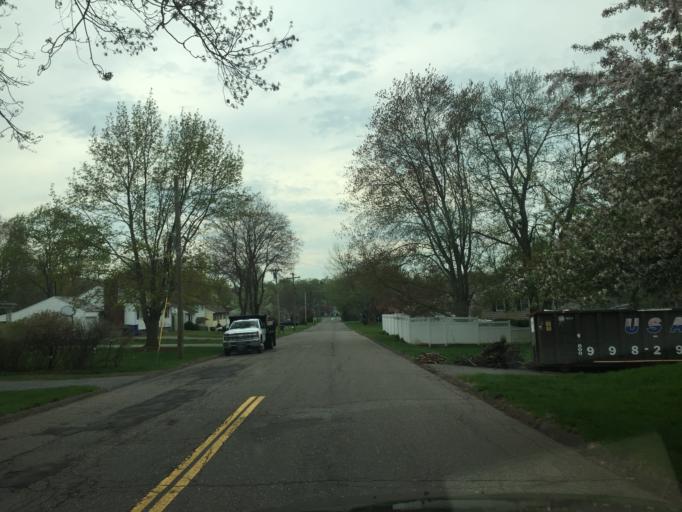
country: US
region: Connecticut
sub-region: Hartford County
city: Newington
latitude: 41.6811
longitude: -72.7262
